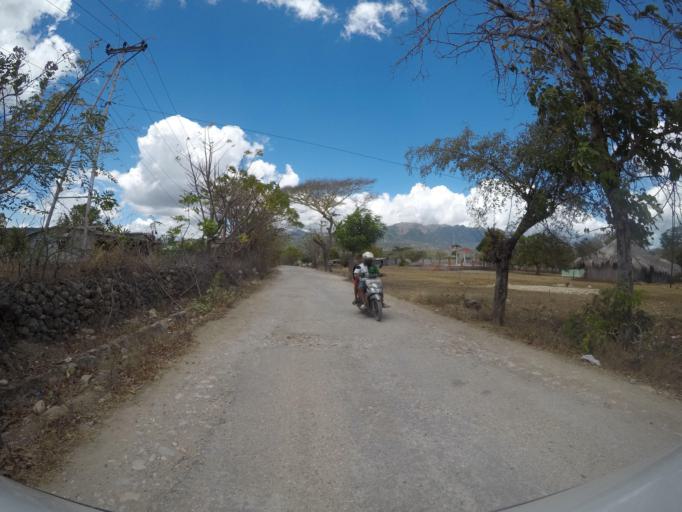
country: TL
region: Baucau
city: Baucau
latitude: -8.4842
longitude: 126.6144
